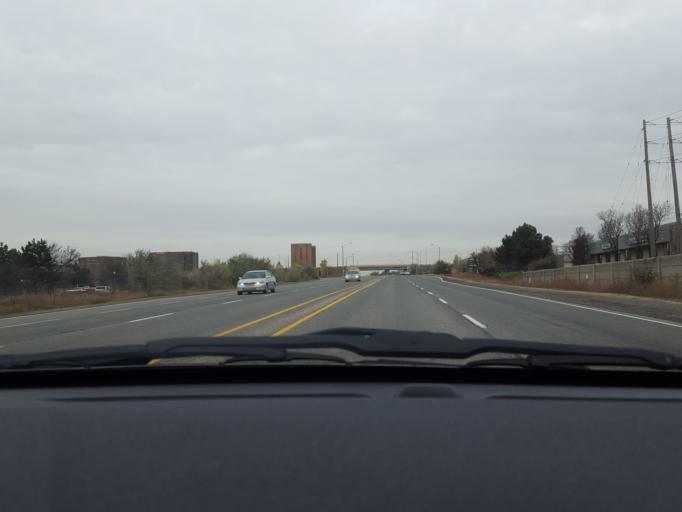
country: CA
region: Ontario
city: Etobicoke
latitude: 43.6848
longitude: -79.5806
